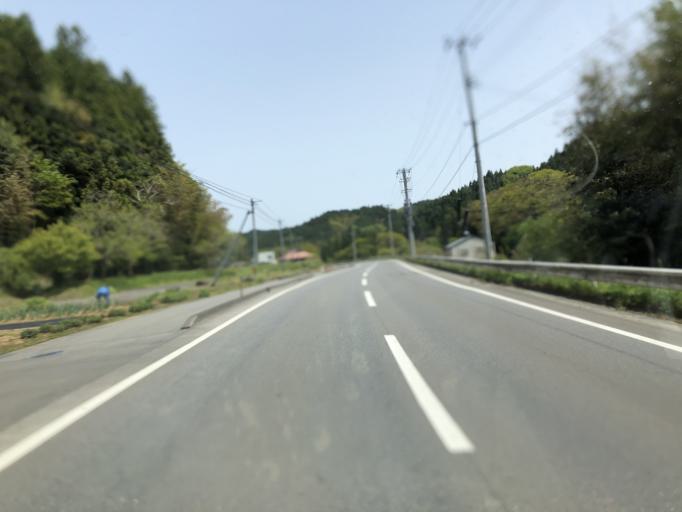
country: JP
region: Fukushima
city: Ishikawa
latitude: 37.0133
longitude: 140.3451
